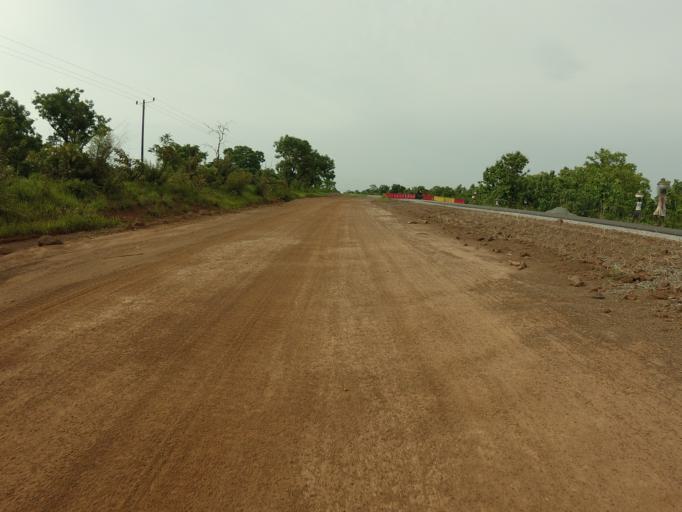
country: GH
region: Northern
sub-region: Yendi
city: Yendi
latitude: 9.6486
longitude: -0.0691
